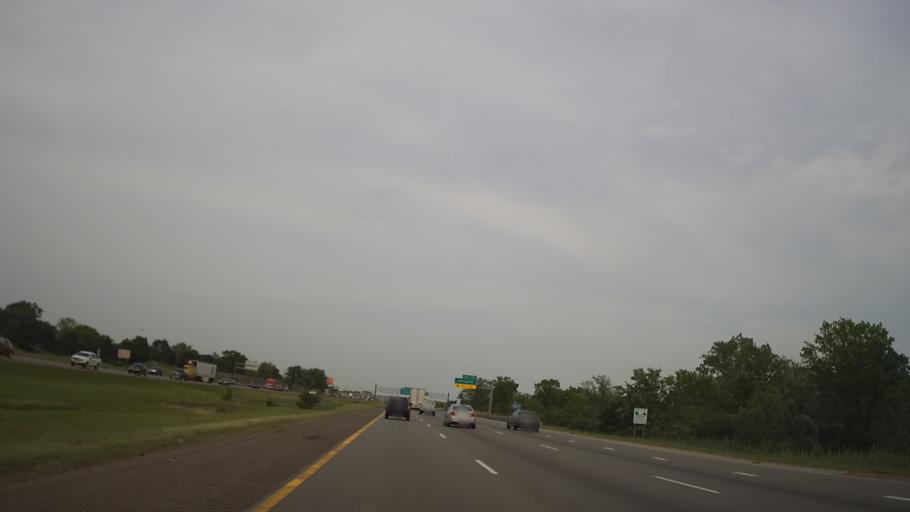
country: US
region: Michigan
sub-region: Wayne County
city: Romulus
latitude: 42.2288
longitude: -83.3825
